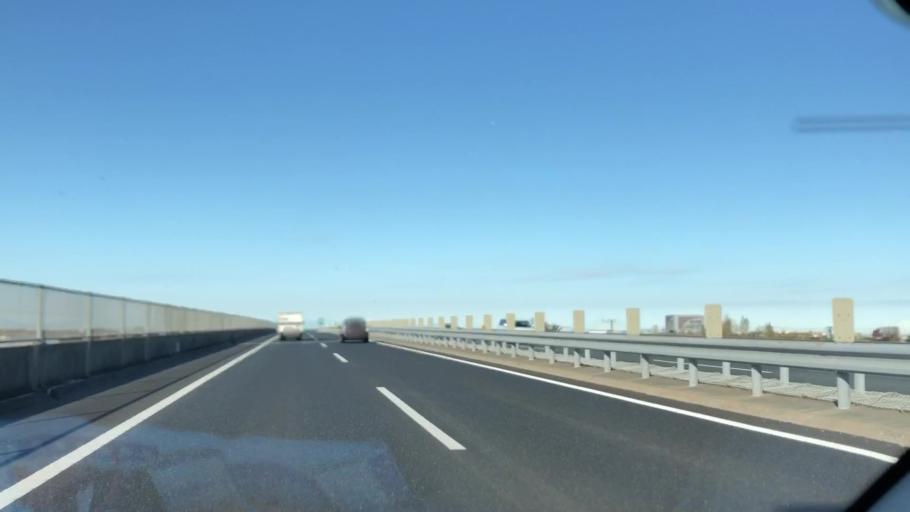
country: JP
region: Chiba
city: Kisarazu
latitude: 35.4178
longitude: 139.9447
